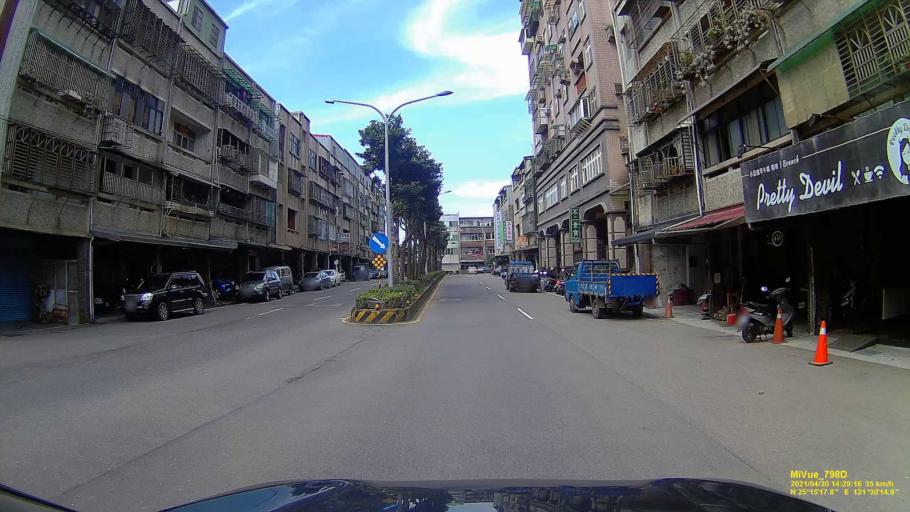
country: TW
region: Taipei
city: Taipei
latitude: 25.2551
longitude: 121.5043
